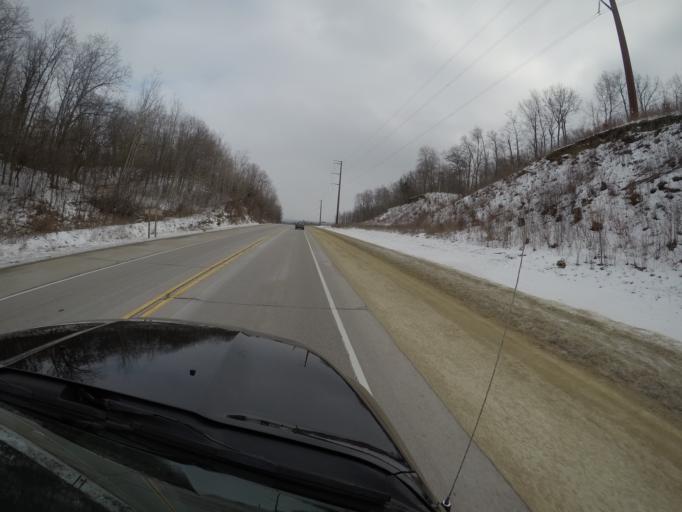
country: US
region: Wisconsin
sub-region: Trempealeau County
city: Galesville
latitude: 44.0719
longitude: -91.3249
